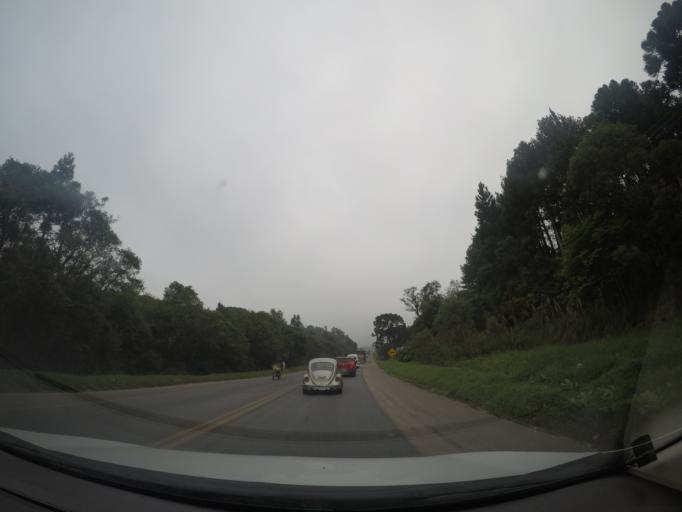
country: BR
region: Parana
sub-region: Almirante Tamandare
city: Almirante Tamandare
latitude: -25.3278
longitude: -49.2948
